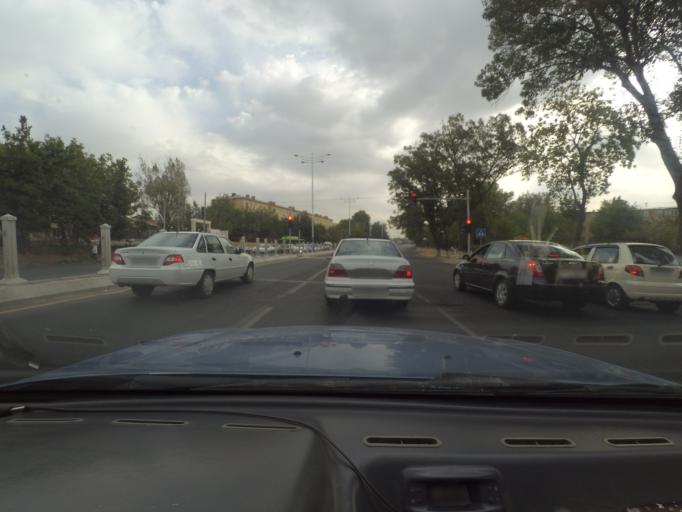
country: UZ
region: Toshkent
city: Salor
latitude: 41.3569
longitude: 69.3791
